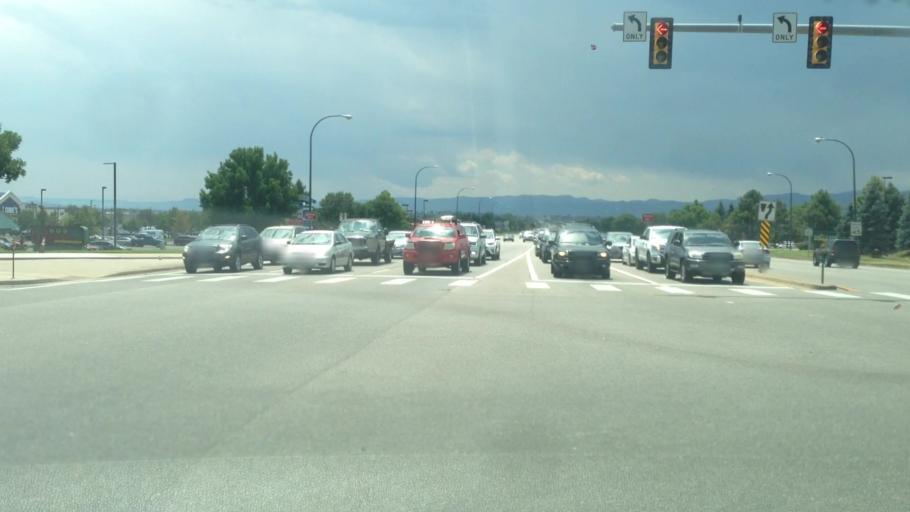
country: US
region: Colorado
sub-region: Jefferson County
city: Columbine
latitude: 39.6243
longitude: -105.0912
